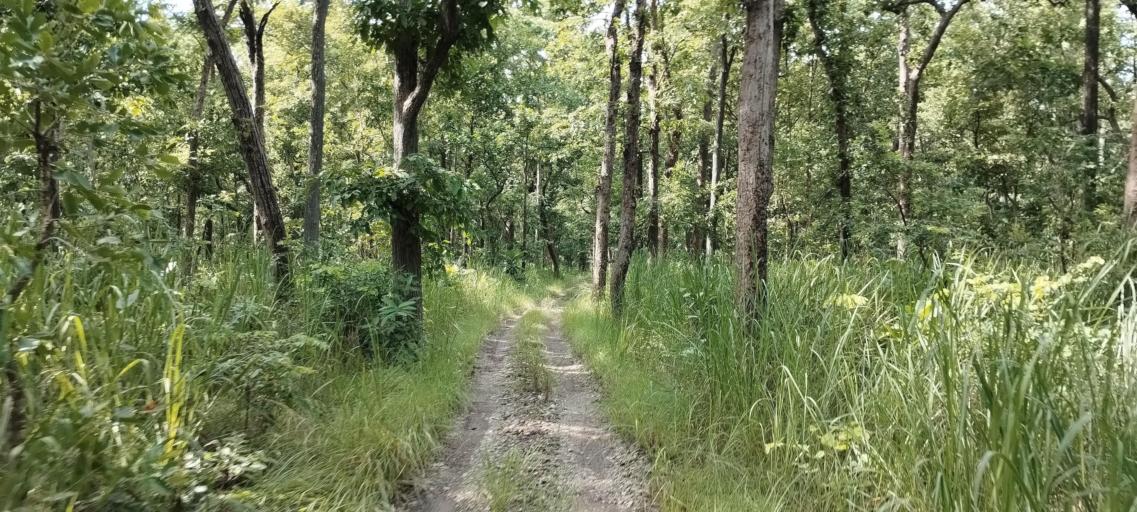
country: NP
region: Far Western
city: Tikapur
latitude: 28.5653
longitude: 81.2932
